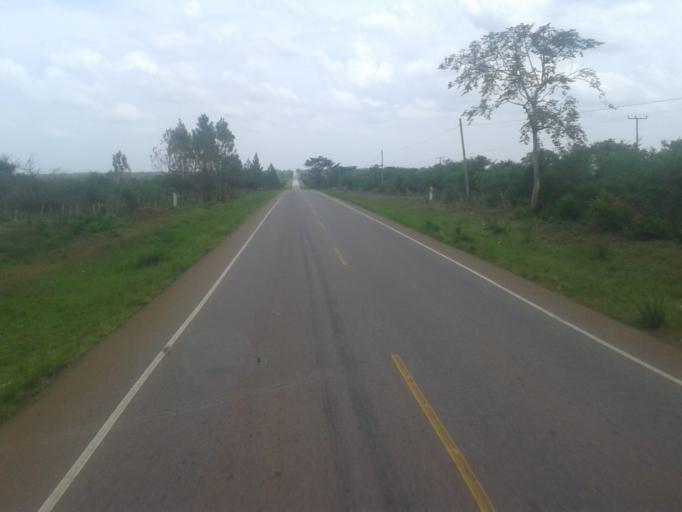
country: UG
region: Central Region
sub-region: Nakasongola District
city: Nakasongola
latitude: 1.3823
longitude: 32.3363
